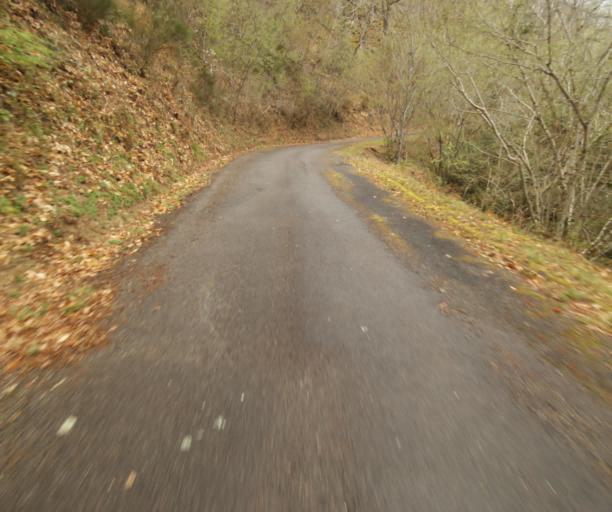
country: FR
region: Limousin
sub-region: Departement de la Correze
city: Saint-Privat
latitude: 45.2080
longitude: 2.0328
